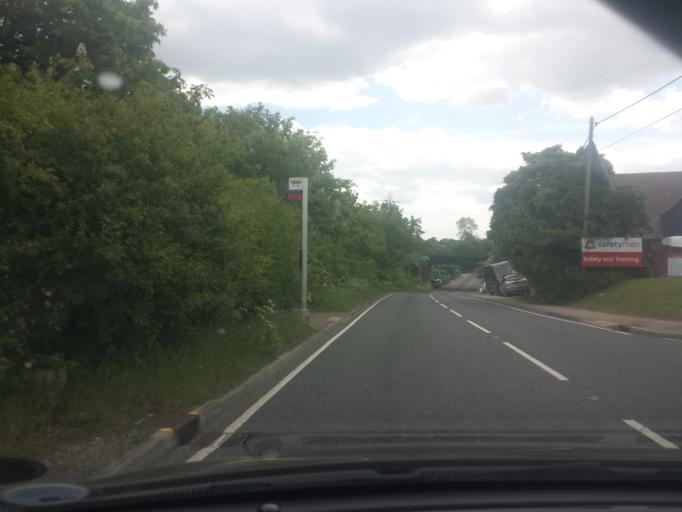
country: GB
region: England
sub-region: Essex
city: Little Clacton
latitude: 51.8486
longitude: 1.1631
